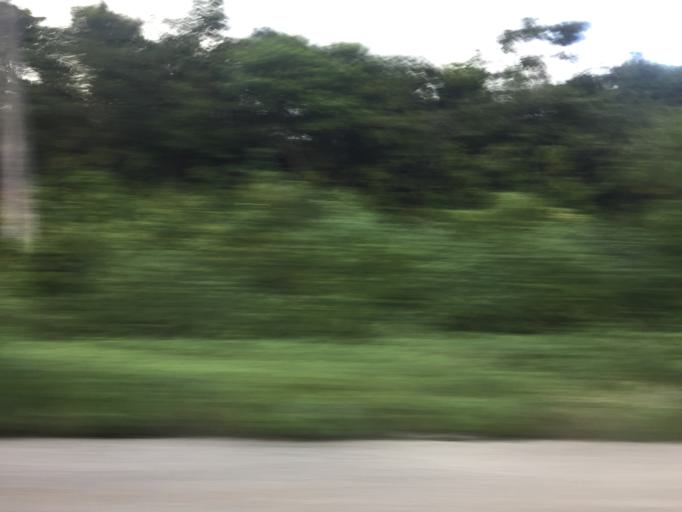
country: MX
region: Quintana Roo
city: Tulum
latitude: 20.2952
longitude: -87.5143
